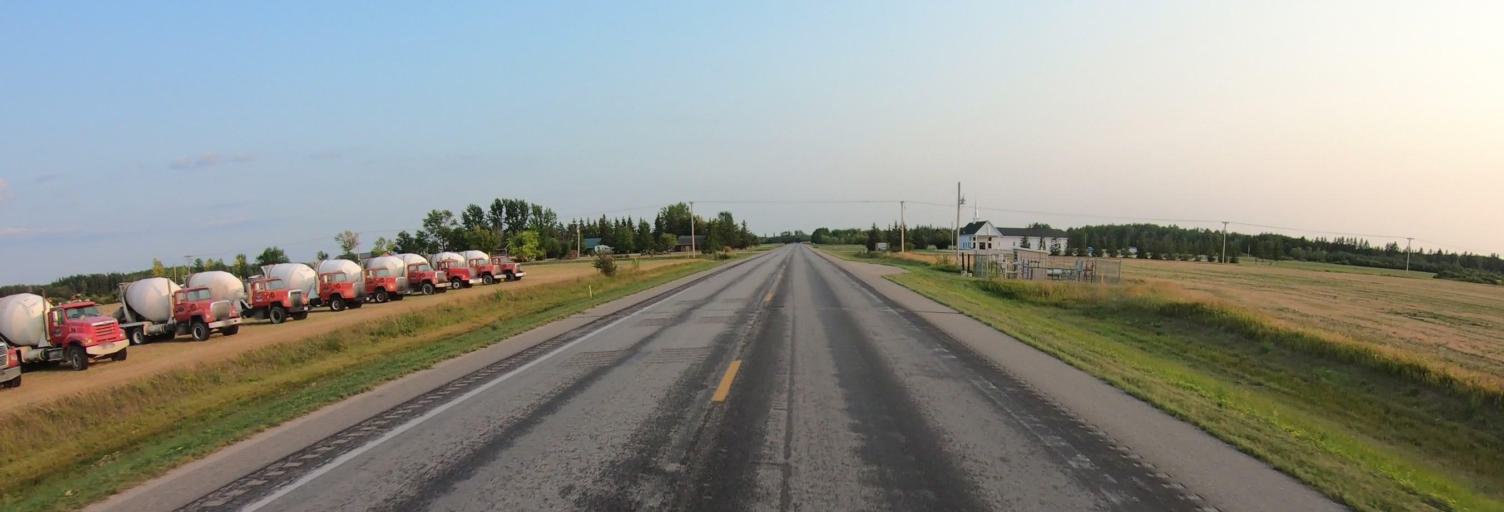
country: US
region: Minnesota
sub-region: Roseau County
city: Warroad
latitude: 48.8957
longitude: -95.3201
